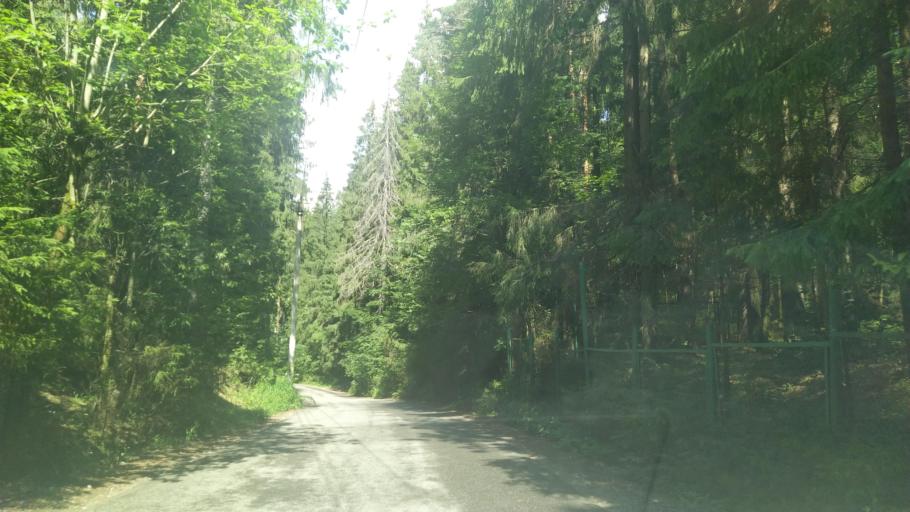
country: RU
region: Leningrad
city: Toksovo
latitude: 60.1694
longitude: 30.5323
